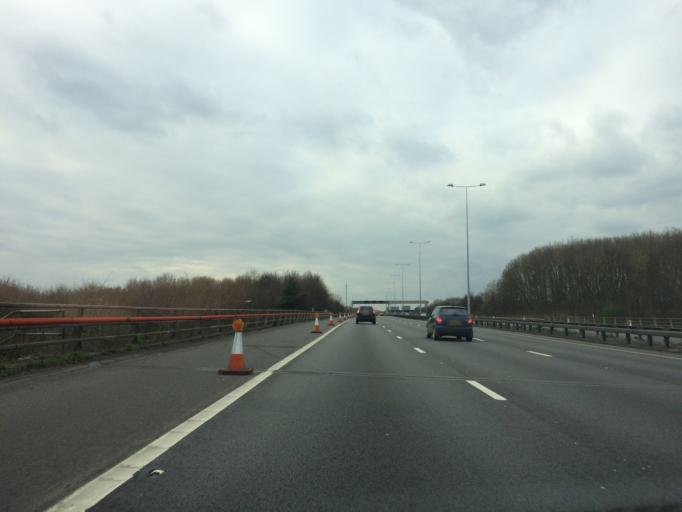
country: GB
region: England
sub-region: Surrey
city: Virginia Water
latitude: 51.3986
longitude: -0.5365
